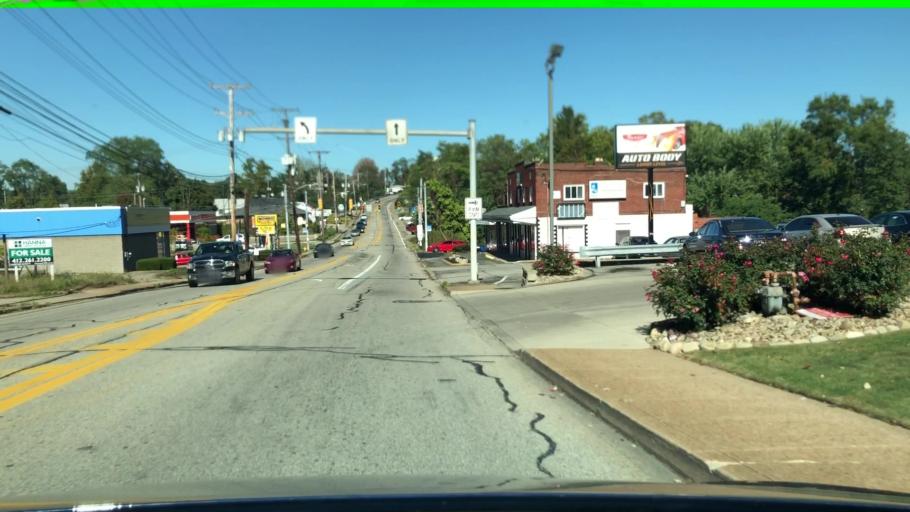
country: US
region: Pennsylvania
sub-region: Allegheny County
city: Churchill
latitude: 40.4676
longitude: -79.8254
